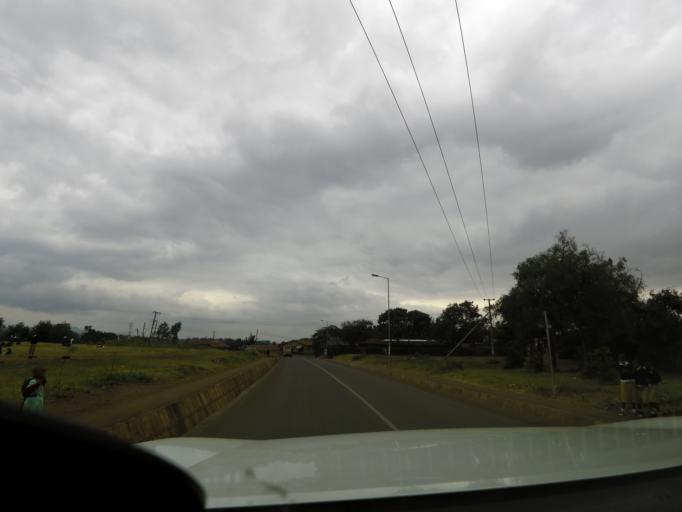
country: TZ
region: Arusha
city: Arusha
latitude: -3.3652
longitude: 36.6607
